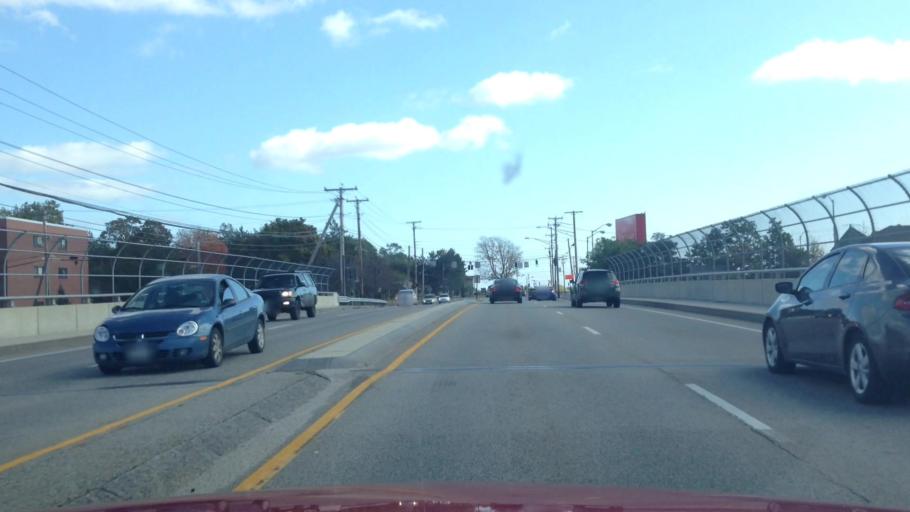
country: US
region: Maine
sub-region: Cumberland County
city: South Portland Gardens
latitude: 43.6765
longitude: -70.3276
